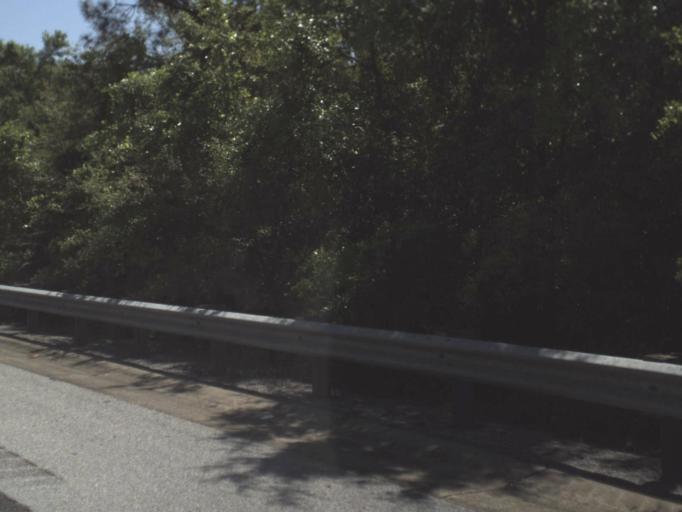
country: US
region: Florida
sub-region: Escambia County
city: Ferry Pass
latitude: 30.5022
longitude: -87.1817
